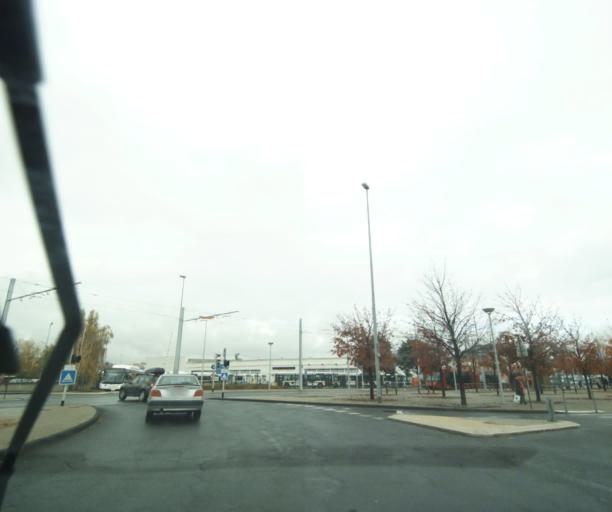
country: FR
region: Auvergne
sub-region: Departement du Puy-de-Dome
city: Aubiere
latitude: 45.7630
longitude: 3.1291
